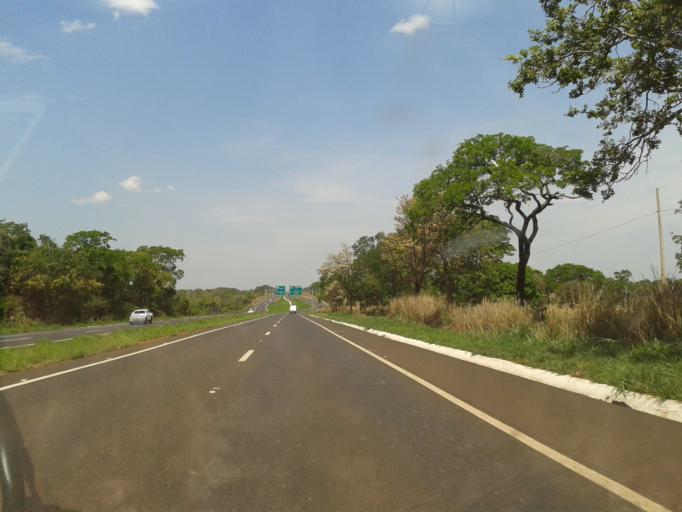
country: BR
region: Minas Gerais
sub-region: Monte Alegre De Minas
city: Monte Alegre de Minas
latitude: -18.8507
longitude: -48.8027
